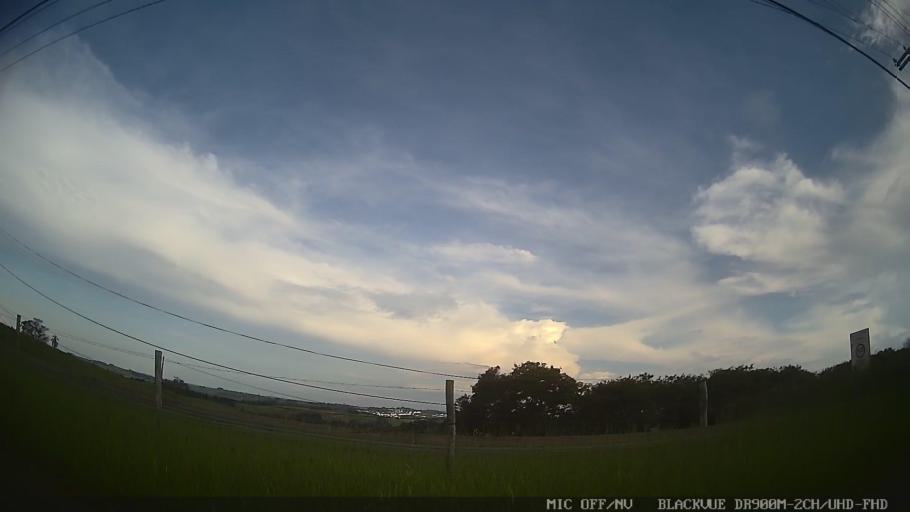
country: BR
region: Sao Paulo
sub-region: Tiete
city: Tiete
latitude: -23.0635
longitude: -47.7278
